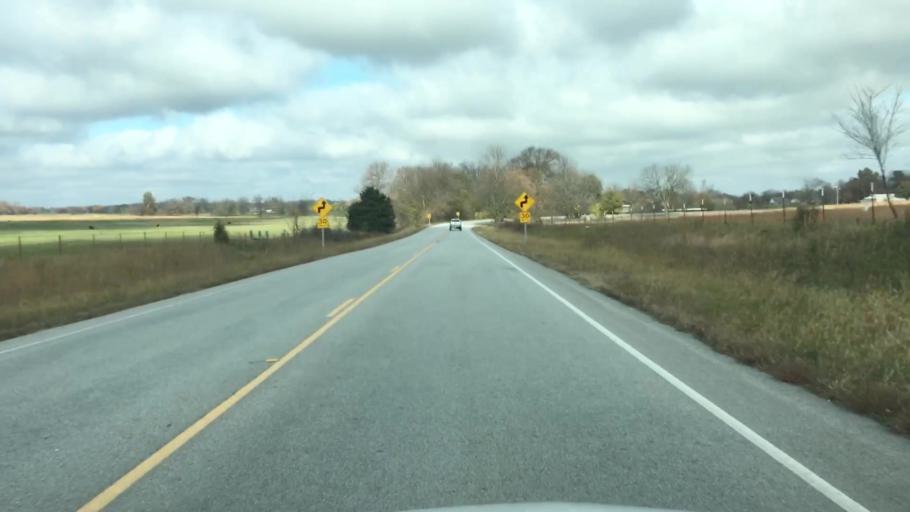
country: US
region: Arkansas
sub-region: Benton County
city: Centerton
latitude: 36.2842
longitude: -94.3501
